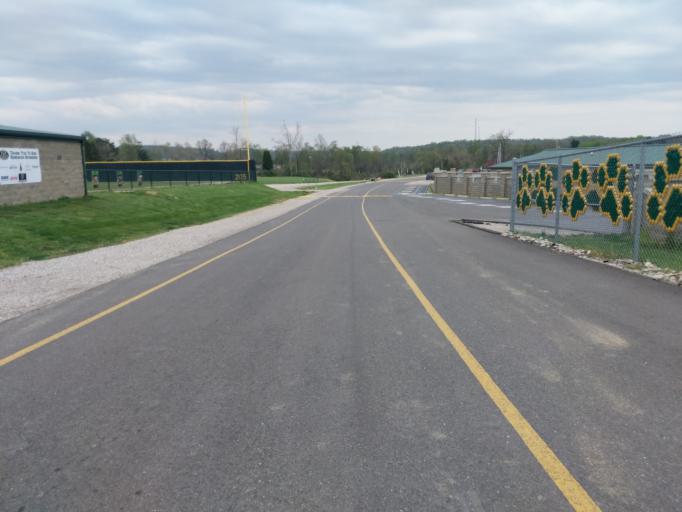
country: US
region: Ohio
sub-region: Athens County
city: The Plains
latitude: 39.3707
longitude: -82.1274
